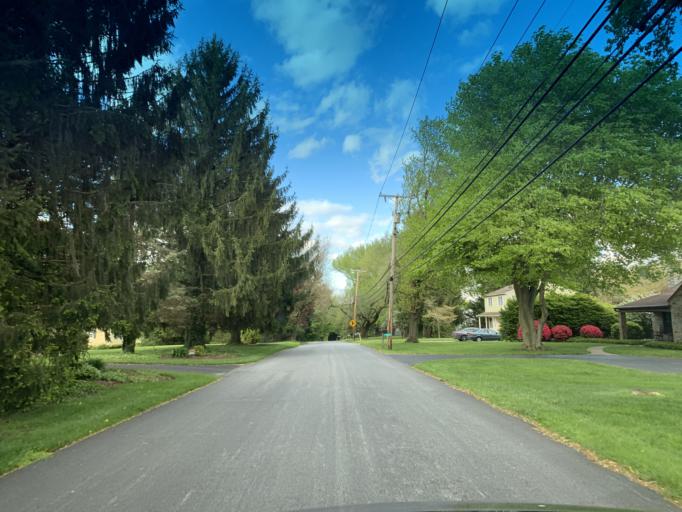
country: US
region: Maryland
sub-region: Baltimore County
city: Hunt Valley
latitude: 39.5268
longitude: -76.5551
